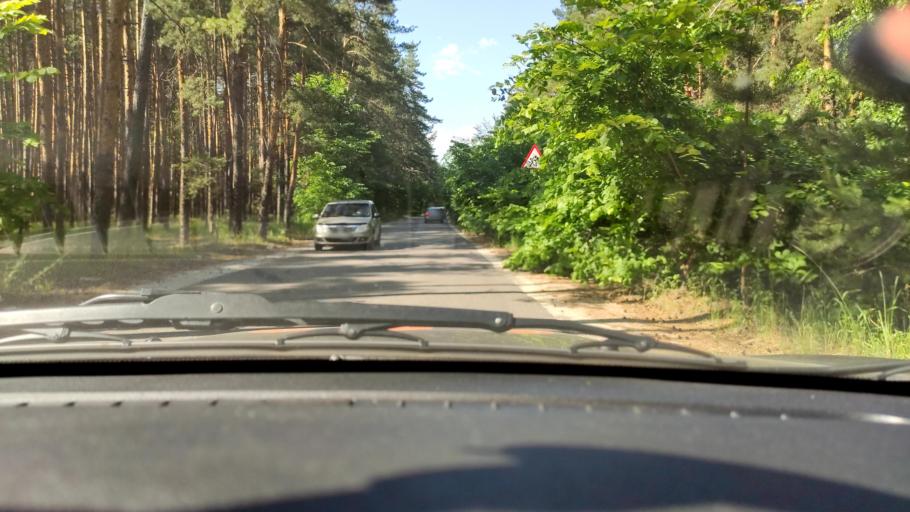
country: RU
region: Voronezj
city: Somovo
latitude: 51.7620
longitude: 39.3656
